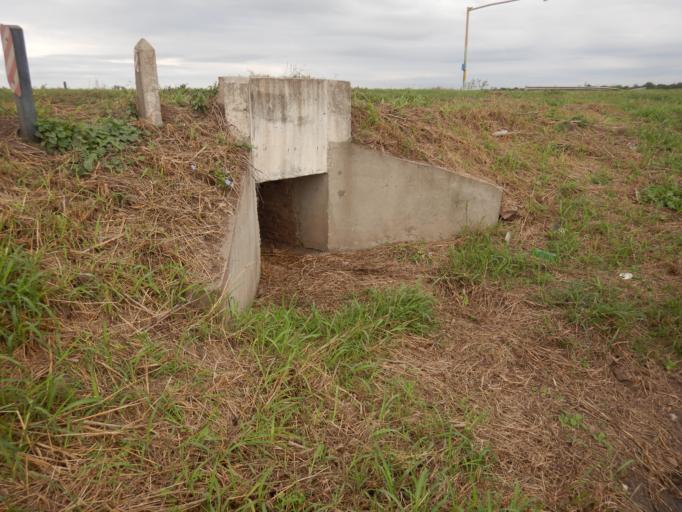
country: AR
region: Santa Fe
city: Roldan
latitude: -32.8899
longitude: -60.9953
